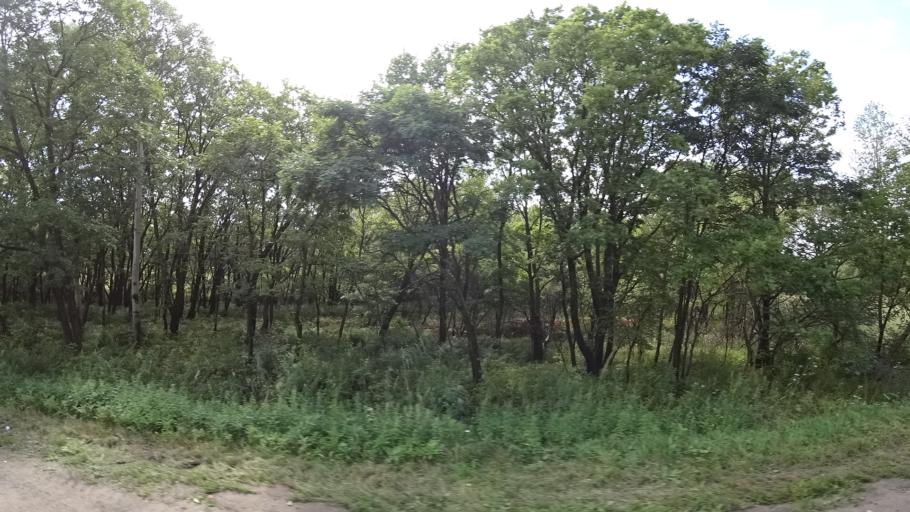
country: RU
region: Primorskiy
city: Lyalichi
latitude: 44.1468
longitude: 132.3990
